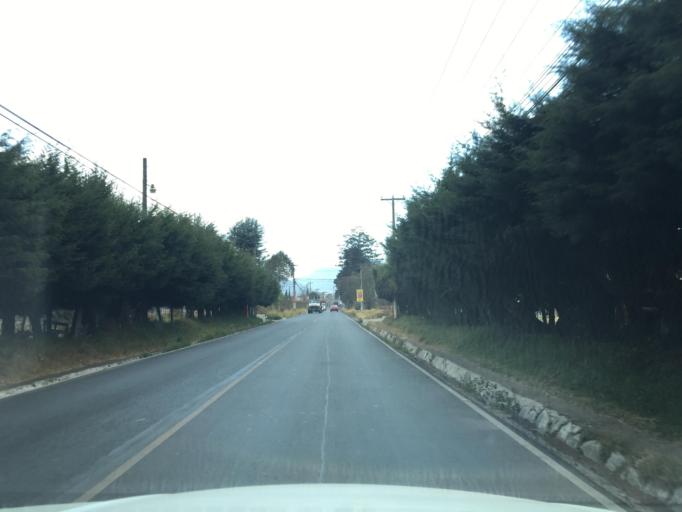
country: GT
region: Quetzaltenango
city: Olintepeque
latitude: 14.8711
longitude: -91.5132
